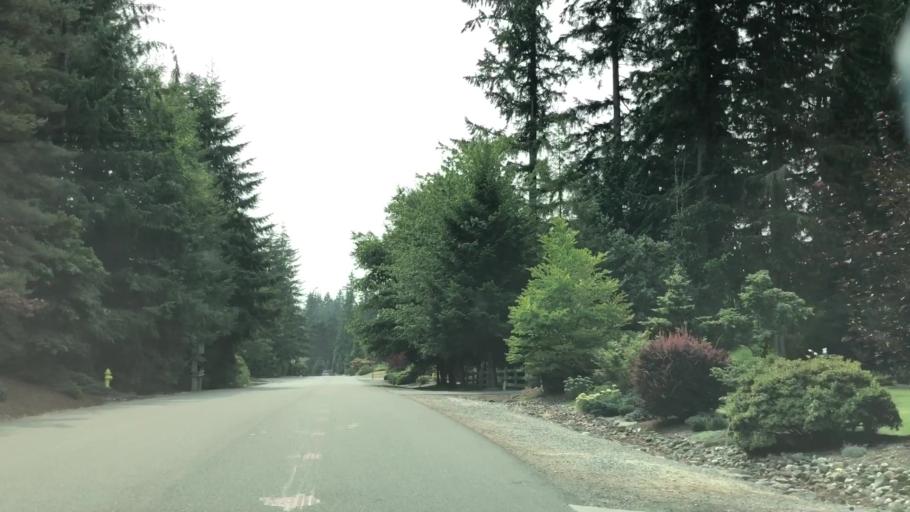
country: US
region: Washington
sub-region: King County
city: Cottage Lake
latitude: 47.7697
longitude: -122.0916
